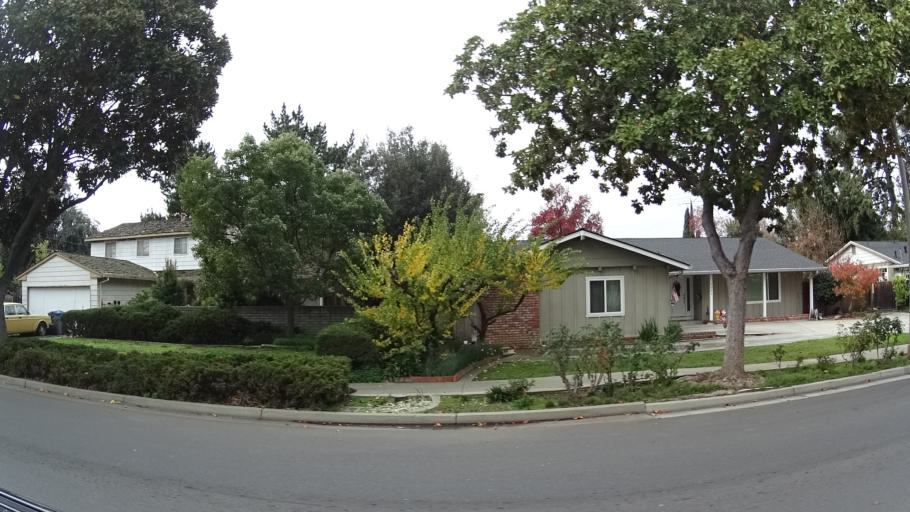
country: US
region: California
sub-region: Santa Clara County
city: Sunnyvale
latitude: 37.3600
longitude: -122.0415
